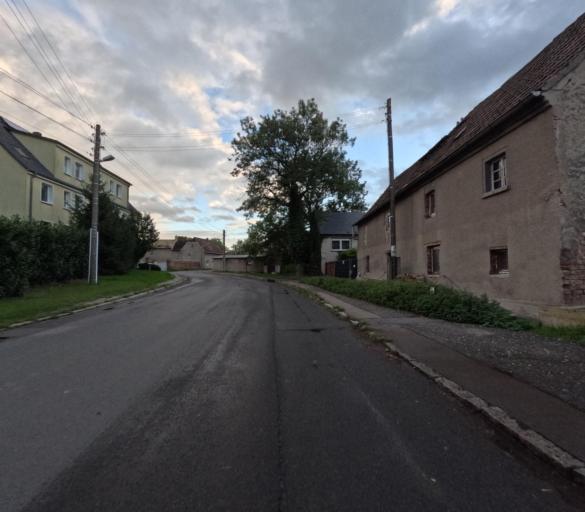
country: DE
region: Saxony
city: Markranstadt
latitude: 51.2736
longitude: 12.2321
